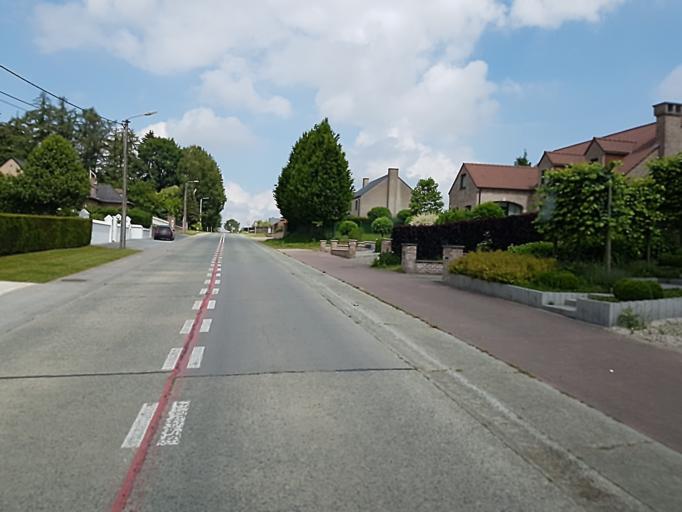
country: BE
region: Wallonia
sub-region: Province du Brabant Wallon
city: Rebecq-Rognon
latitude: 50.7104
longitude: 4.1123
